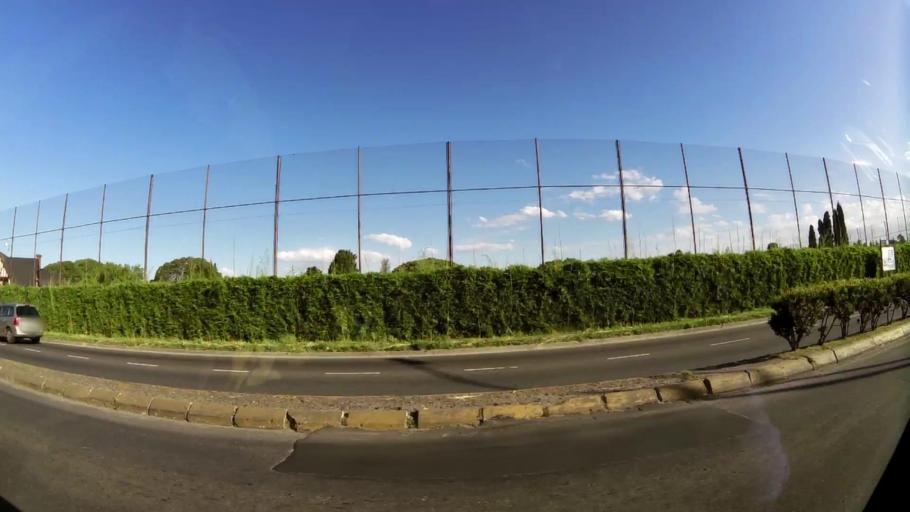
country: AR
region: Buenos Aires
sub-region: Partido de San Isidro
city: San Isidro
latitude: -34.4864
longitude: -58.5355
